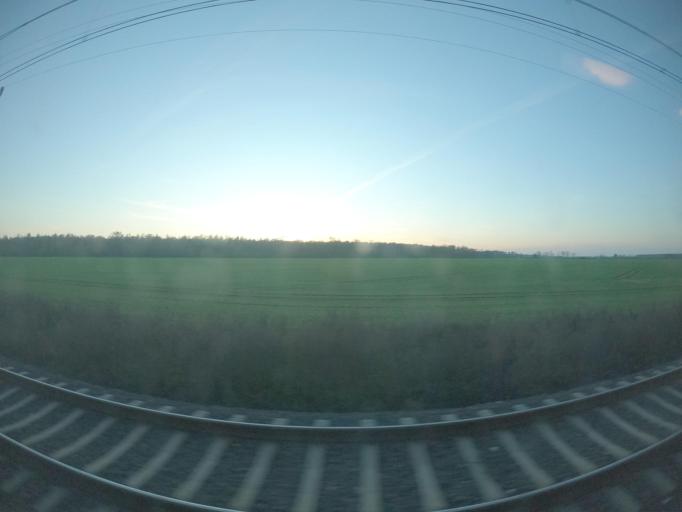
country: PL
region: West Pomeranian Voivodeship
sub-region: Powiat mysliborski
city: Boleszkowice
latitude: 52.7292
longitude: 14.5233
